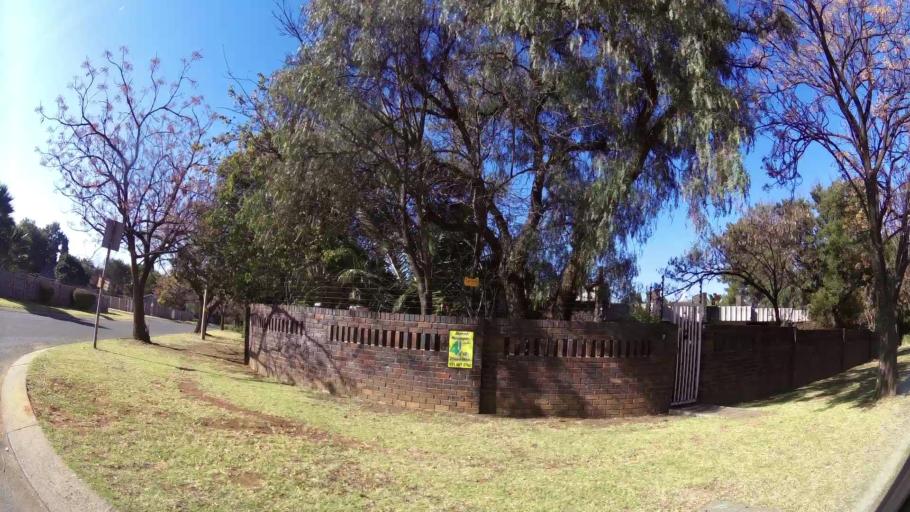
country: ZA
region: Gauteng
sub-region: Ekurhuleni Metropolitan Municipality
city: Germiston
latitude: -26.3314
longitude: 28.1055
